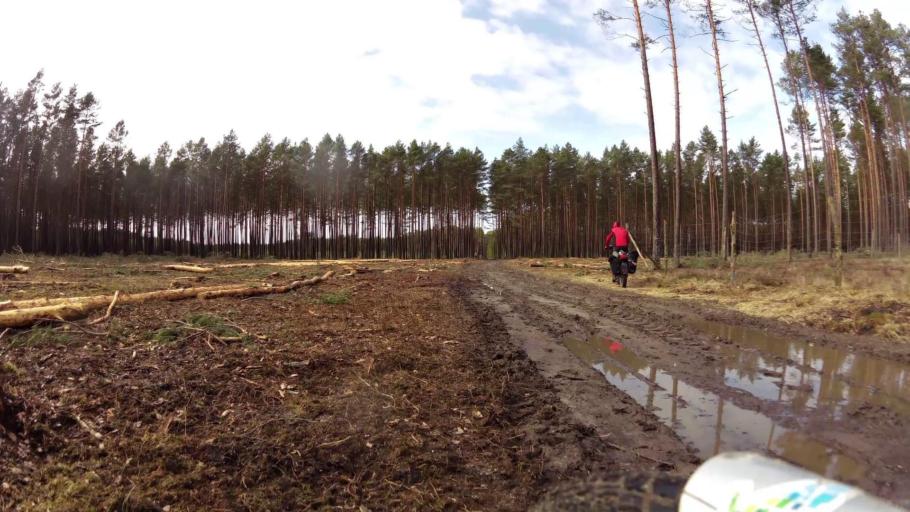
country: PL
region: Pomeranian Voivodeship
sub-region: Powiat bytowski
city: Kolczyglowy
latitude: 54.2006
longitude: 17.2306
